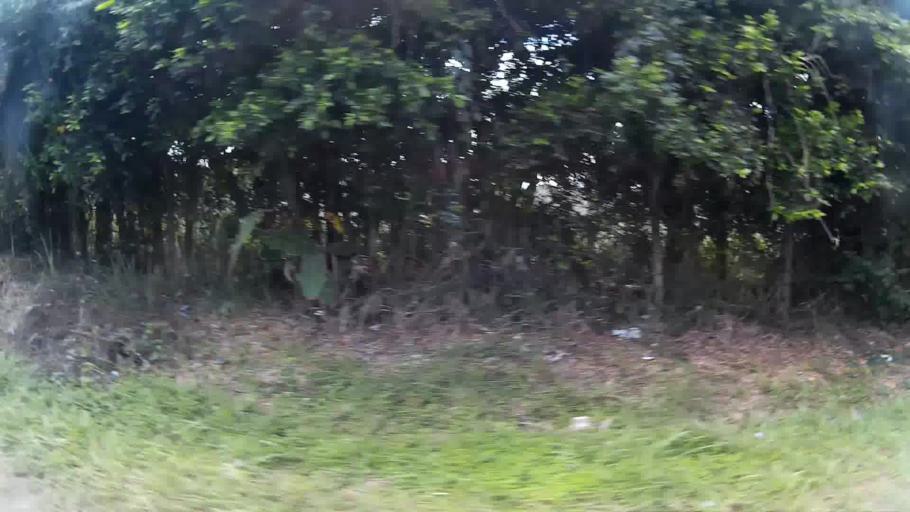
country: CO
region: Risaralda
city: La Virginia
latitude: 4.8273
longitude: -75.8436
